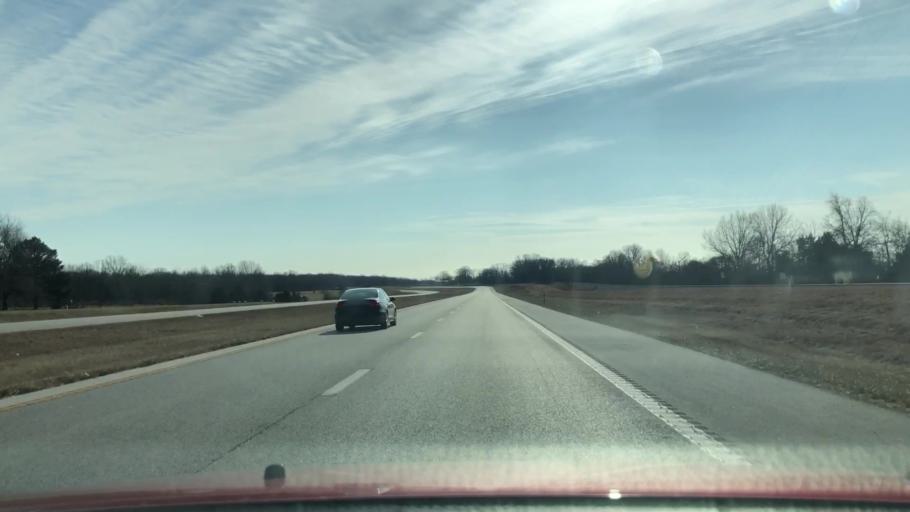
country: US
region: Missouri
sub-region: Webster County
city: Seymour
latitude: 37.1381
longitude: -92.7446
